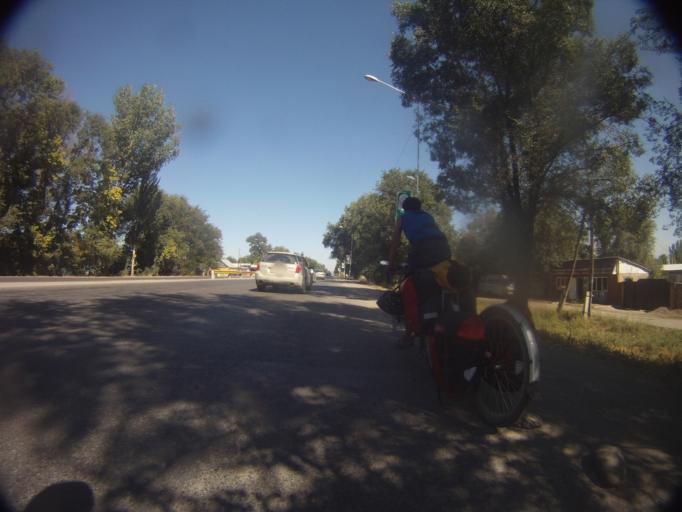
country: KG
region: Chuy
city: Sokuluk
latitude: 42.8726
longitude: 74.4382
